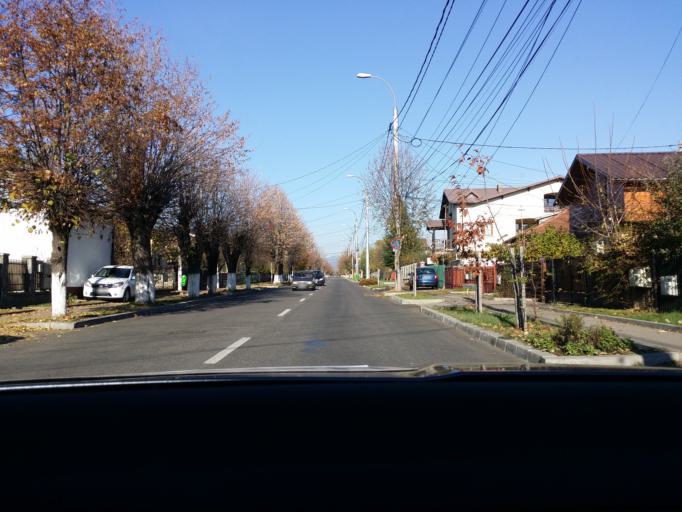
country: RO
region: Prahova
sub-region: Municipiul Campina
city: Campina
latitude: 45.1362
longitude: 25.7274
